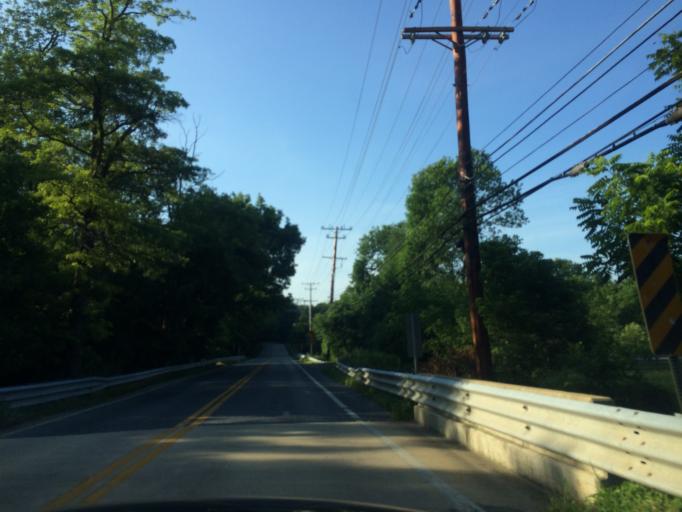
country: US
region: Maryland
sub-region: Howard County
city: Highland
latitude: 39.1949
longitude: -76.9359
